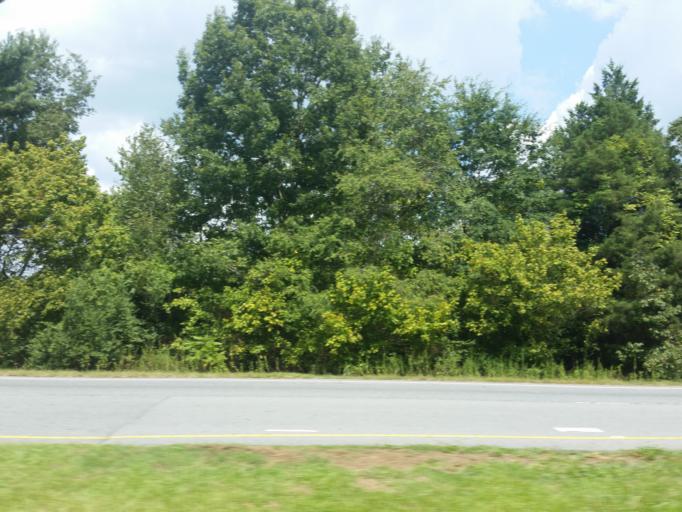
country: US
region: North Carolina
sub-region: Cleveland County
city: White Plains
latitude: 35.2585
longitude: -81.4602
